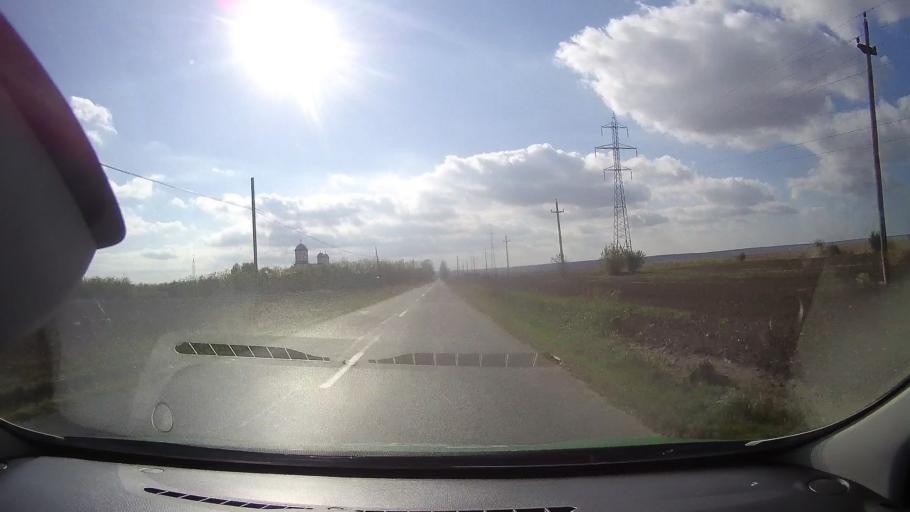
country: RO
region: Constanta
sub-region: Comuna Istria
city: Istria
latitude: 44.5474
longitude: 28.6933
